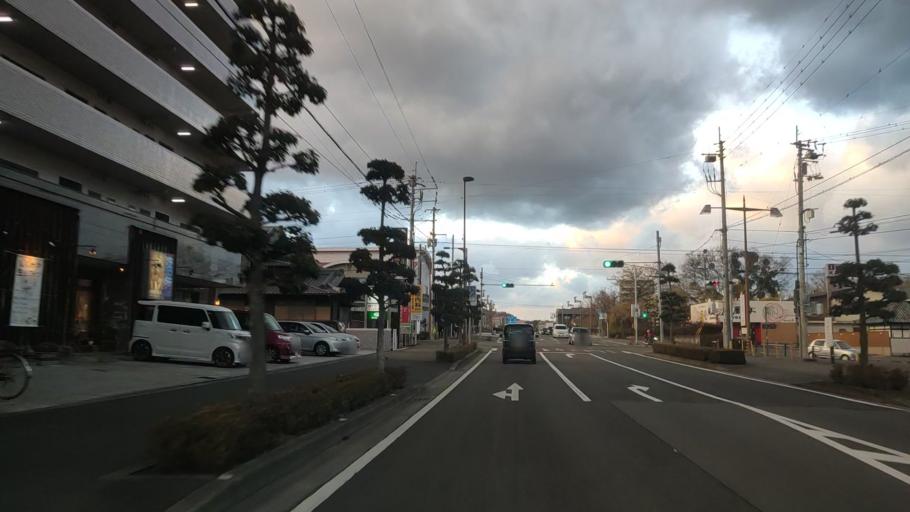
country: JP
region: Ehime
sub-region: Shikoku-chuo Shi
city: Matsuyama
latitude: 33.8384
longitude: 132.7865
